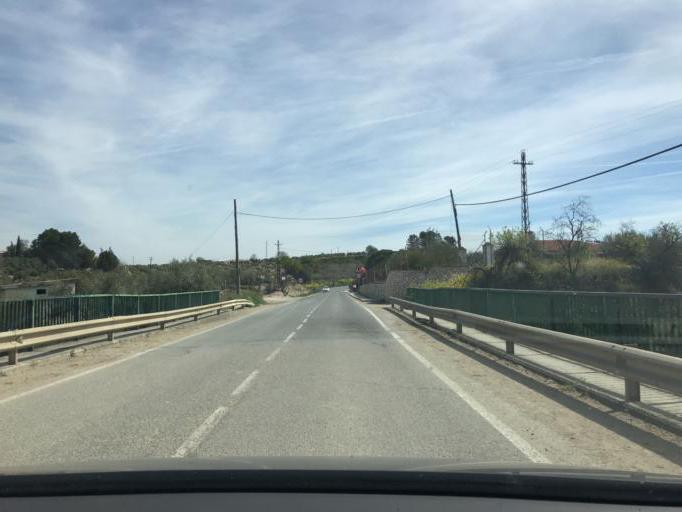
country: ES
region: Andalusia
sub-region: Provincia de Jaen
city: Porcuna
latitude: 37.8730
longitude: -4.1714
